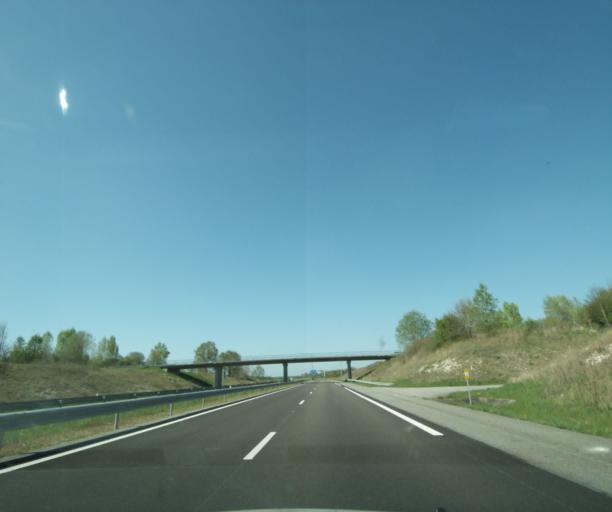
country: FR
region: Centre
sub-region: Departement du Loiret
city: Bonny-sur-Loire
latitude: 47.5646
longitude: 2.8805
